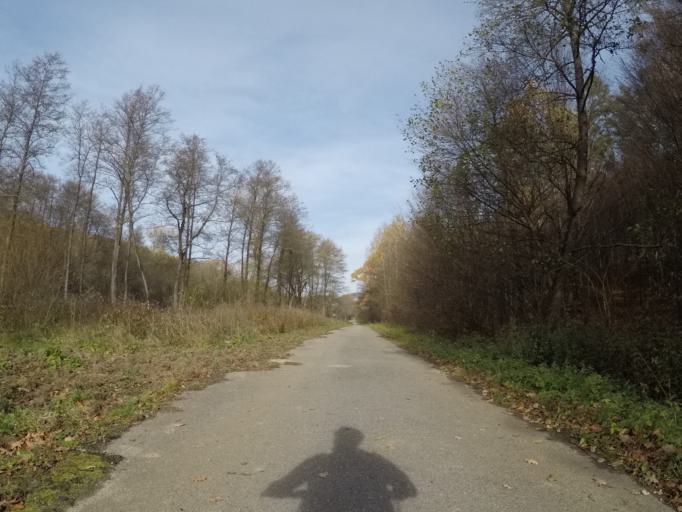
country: SK
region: Presovsky
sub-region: Okres Presov
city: Presov
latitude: 48.9647
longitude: 21.1927
